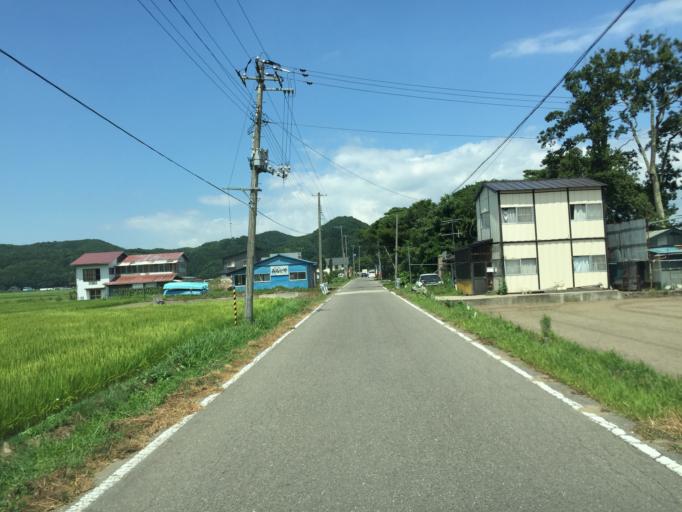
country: JP
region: Fukushima
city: Inawashiro
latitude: 37.4590
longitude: 140.0466
